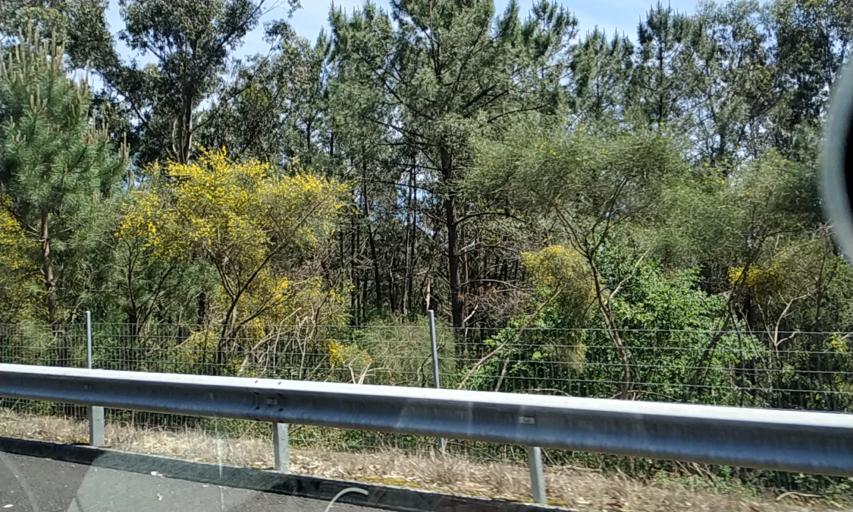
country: ES
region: Galicia
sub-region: Provincia de Pontevedra
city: Portas
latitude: 42.6069
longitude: -8.6682
